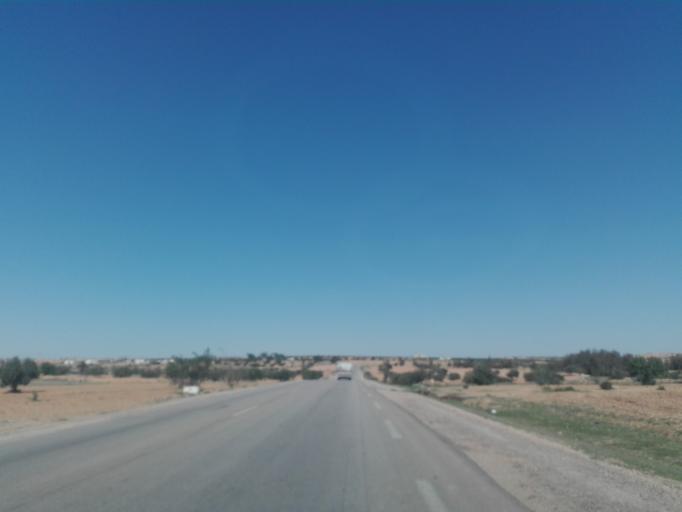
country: TN
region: Safaqis
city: Bi'r `Ali Bin Khalifah
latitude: 34.7438
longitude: 10.3653
